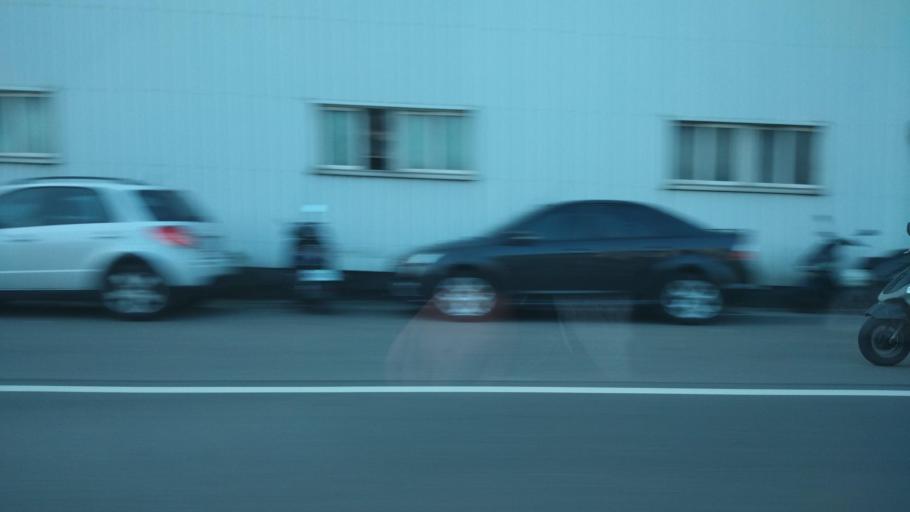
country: TW
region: Taipei
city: Taipei
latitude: 25.2483
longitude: 121.4624
